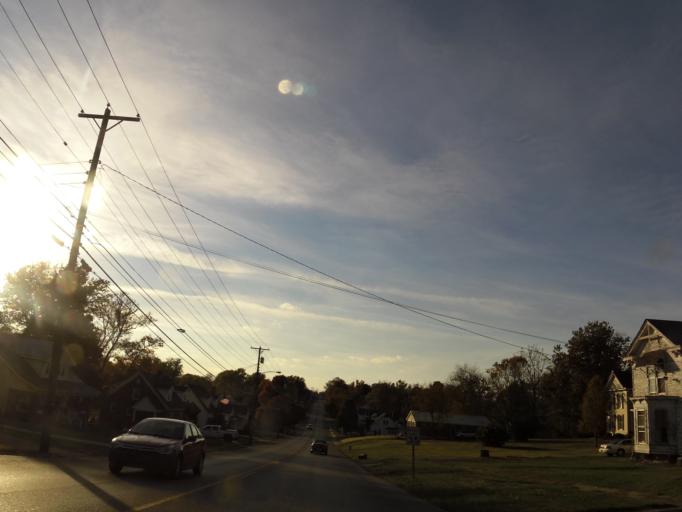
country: US
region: Kentucky
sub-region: Garrard County
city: Lancaster
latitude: 37.6197
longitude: -84.5821
